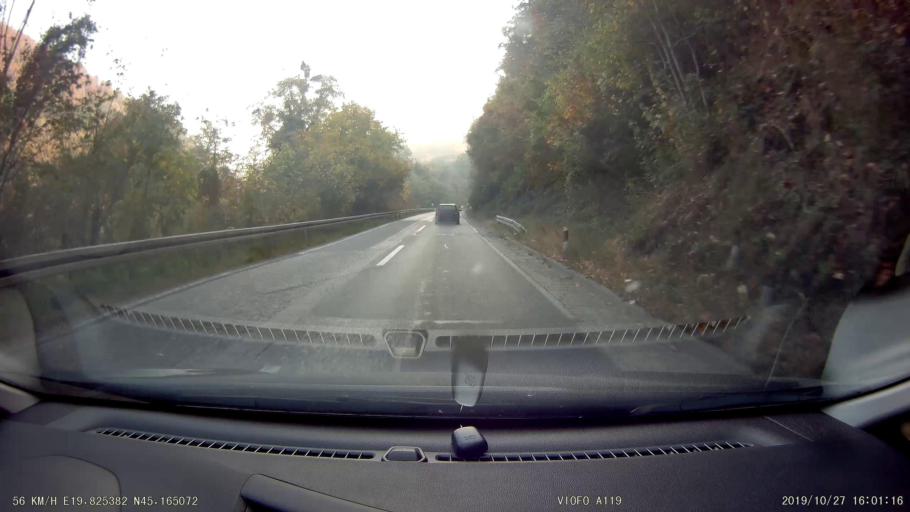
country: RS
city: Vrdnik
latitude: 45.1650
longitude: 19.8254
